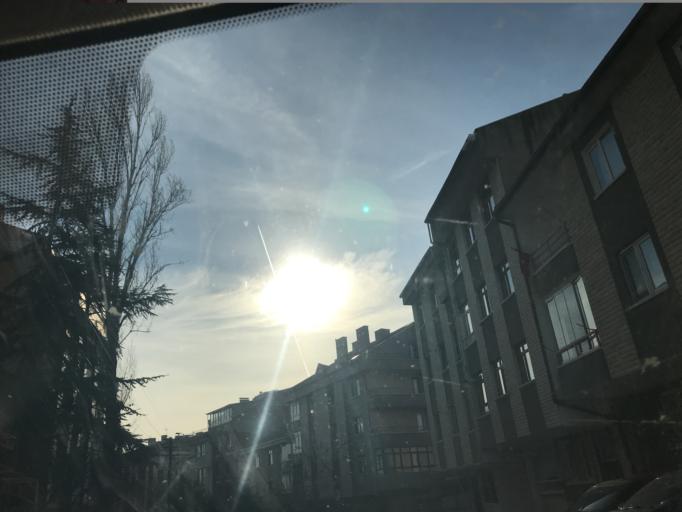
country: TR
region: Ankara
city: Ankara
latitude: 39.9671
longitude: 32.8020
